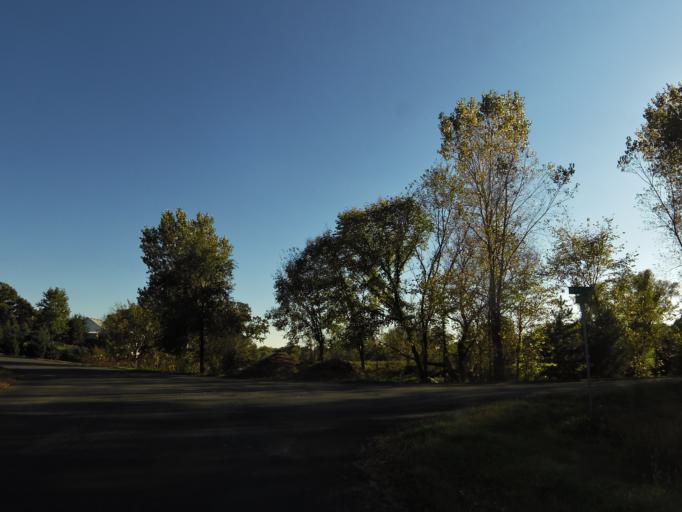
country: US
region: Minnesota
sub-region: Washington County
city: Lakeland
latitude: 44.9766
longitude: -92.8029
